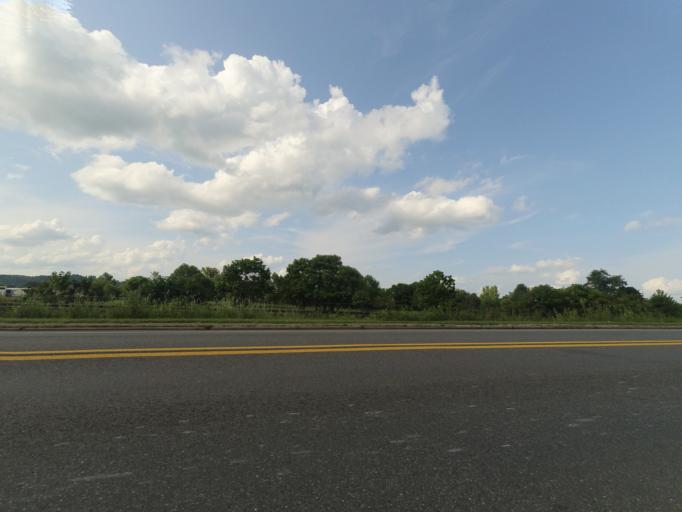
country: US
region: West Virginia
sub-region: Cabell County
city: Huntington
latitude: 38.4225
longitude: -82.4024
